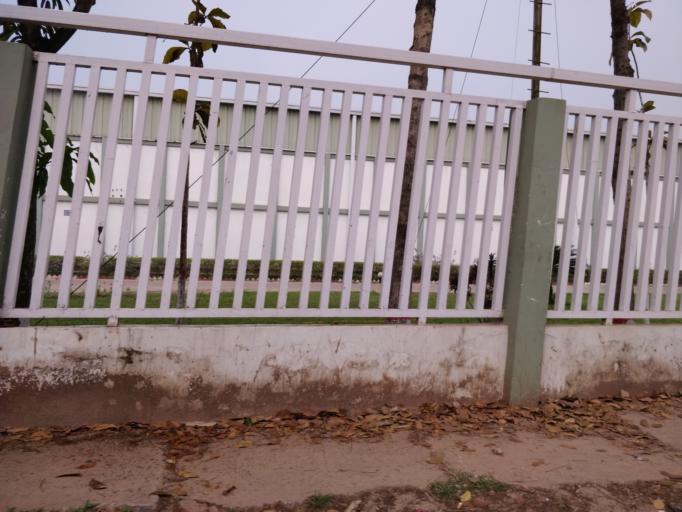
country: BD
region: Sylhet
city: Habiganj
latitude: 24.1712
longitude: 91.3552
